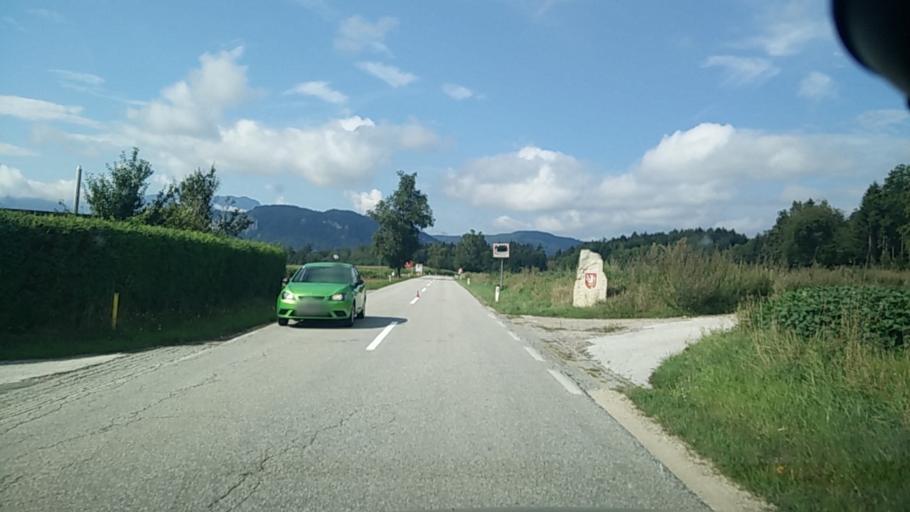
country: AT
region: Carinthia
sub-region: Politischer Bezirk Klagenfurt Land
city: Grafenstein
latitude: 46.6222
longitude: 14.5280
